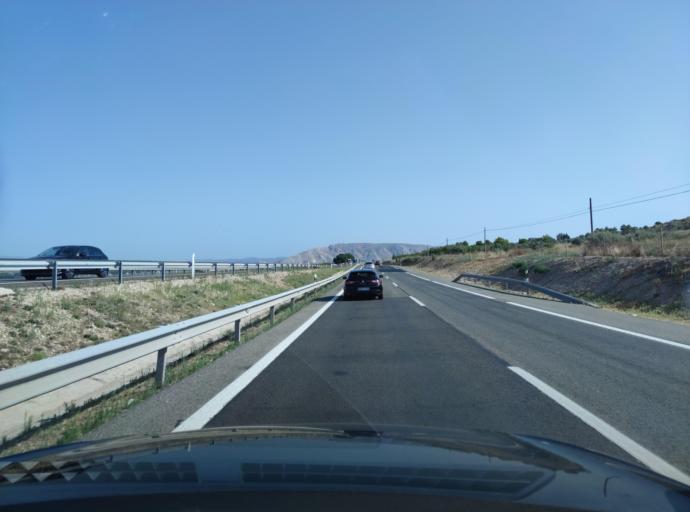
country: ES
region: Valencia
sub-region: Provincia de Alicante
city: Sax
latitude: 38.5839
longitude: -0.8434
